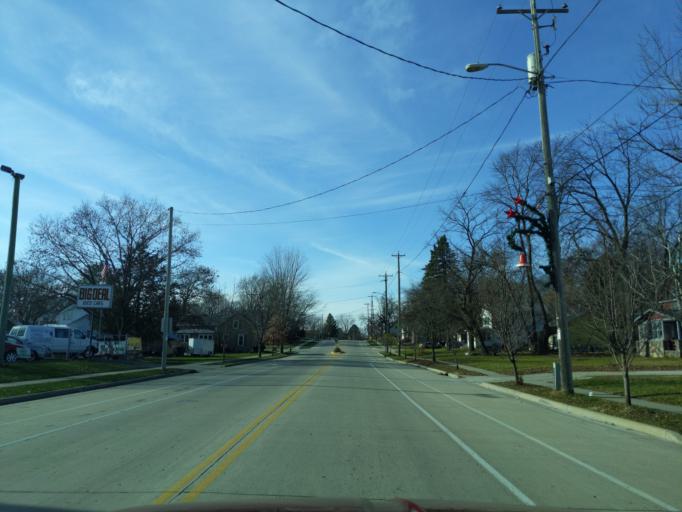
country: US
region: Wisconsin
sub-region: Walworth County
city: Whitewater
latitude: 42.8327
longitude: -88.7216
